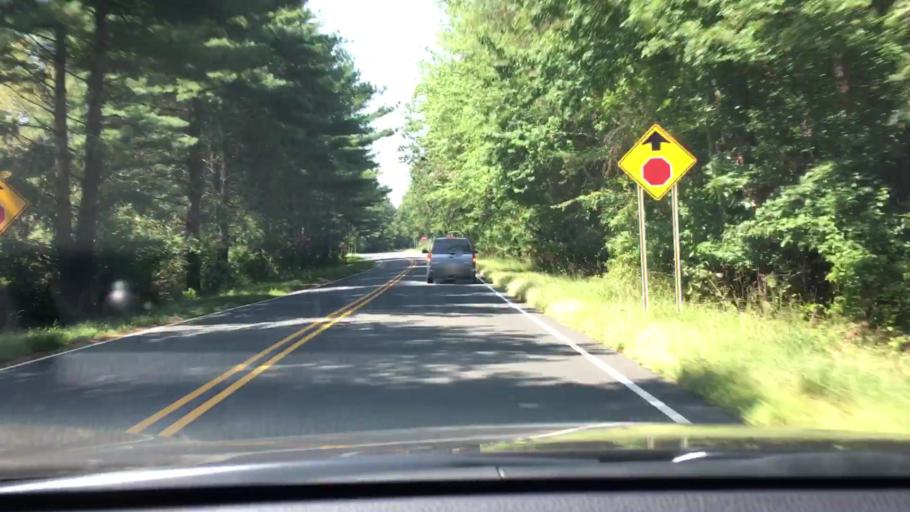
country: US
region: New Jersey
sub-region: Cumberland County
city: Port Norris
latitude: 39.2594
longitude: -74.9286
